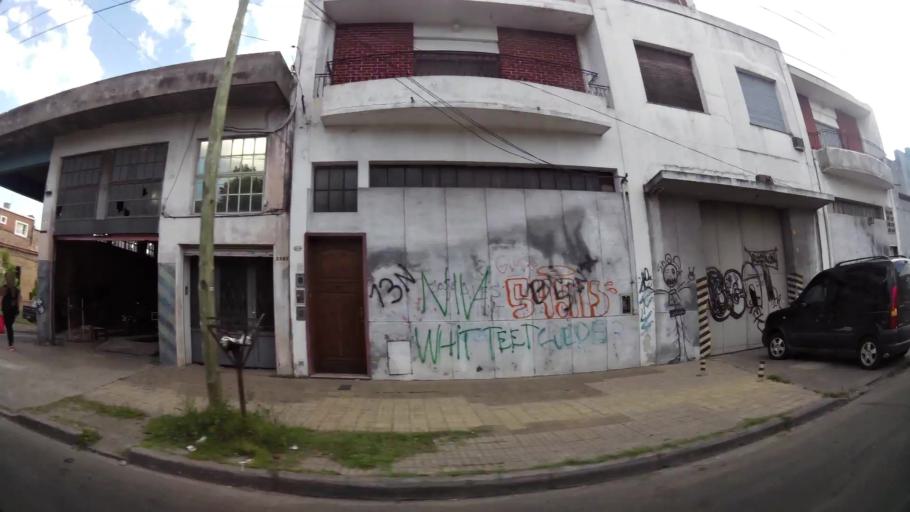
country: AR
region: Buenos Aires
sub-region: Partido de Avellaneda
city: Avellaneda
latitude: -34.6783
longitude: -58.3541
